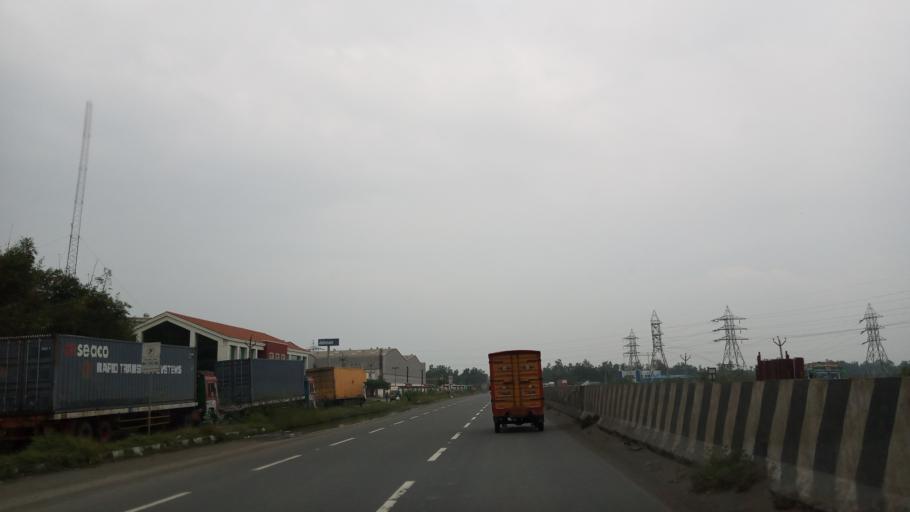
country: IN
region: Tamil Nadu
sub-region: Kancheepuram
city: Madambakkam
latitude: 12.8541
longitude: 79.9480
